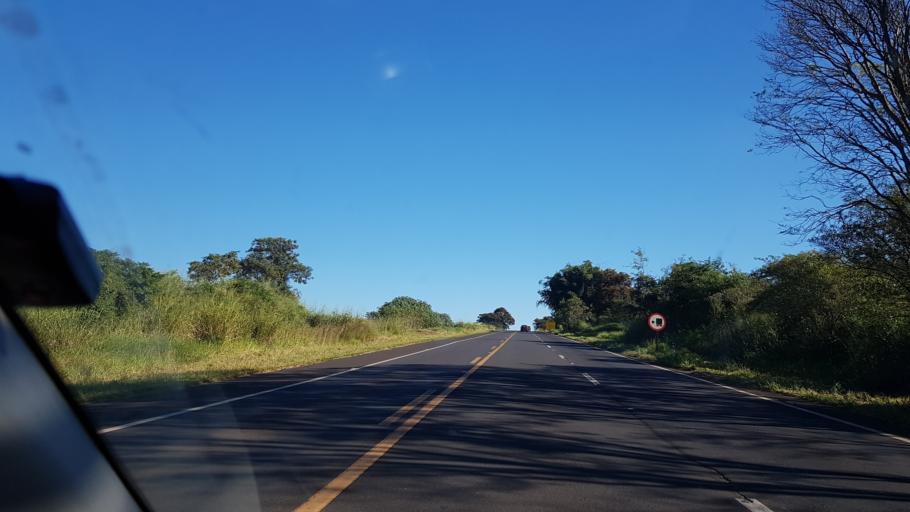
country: BR
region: Sao Paulo
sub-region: Assis
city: Assis
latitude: -22.6005
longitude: -50.4802
